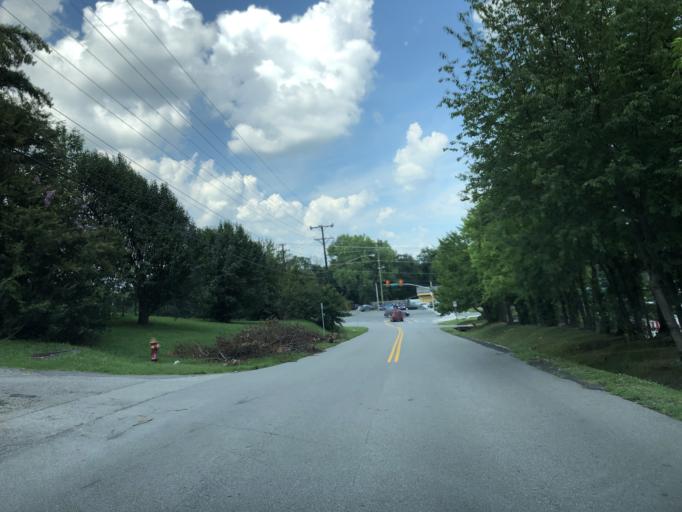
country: US
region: Tennessee
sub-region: Davidson County
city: Nashville
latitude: 36.1304
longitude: -86.7178
